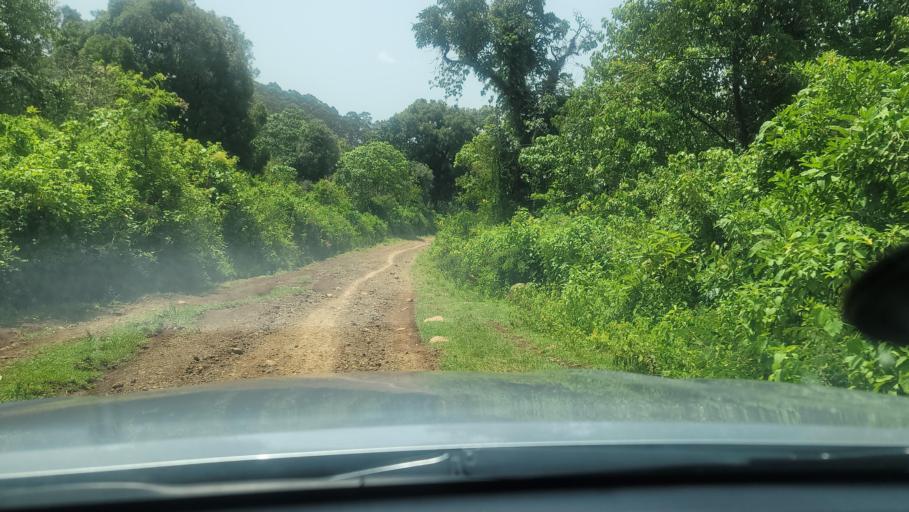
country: ET
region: Oromiya
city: Agaro
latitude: 7.8173
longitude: 36.4124
